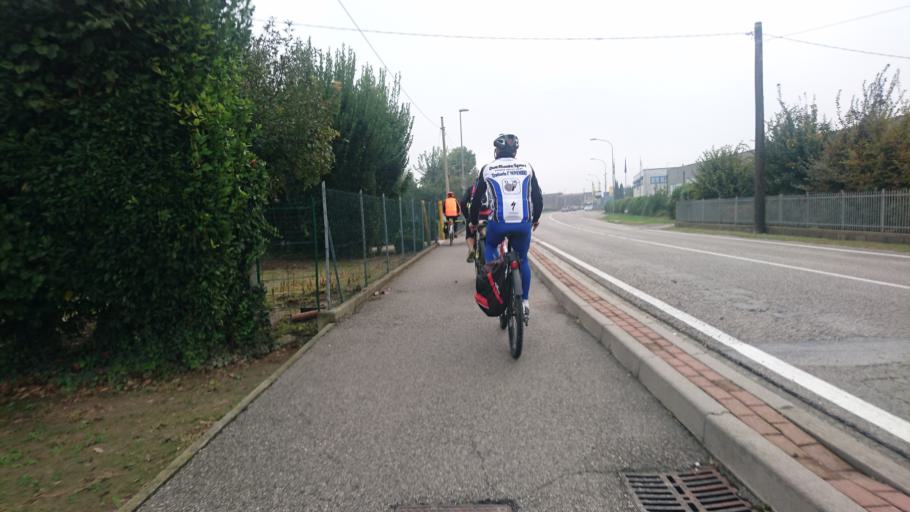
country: IT
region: Veneto
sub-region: Provincia di Padova
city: Pozzonovo
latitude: 45.2058
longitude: 11.7823
